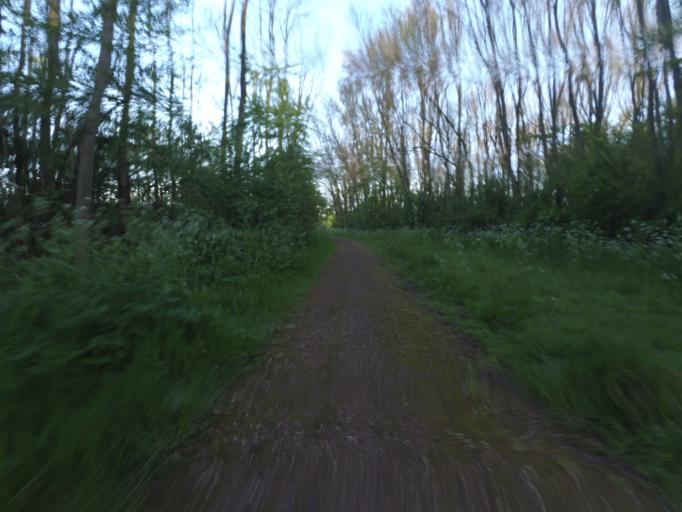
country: NL
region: Flevoland
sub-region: Gemeente Lelystad
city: Lelystad
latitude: 52.4337
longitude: 5.4916
